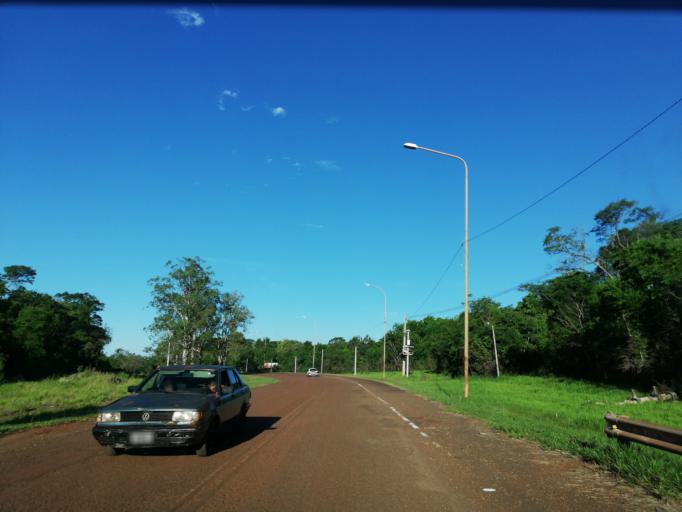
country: AR
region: Misiones
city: Garupa
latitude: -27.4605
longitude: -55.8184
